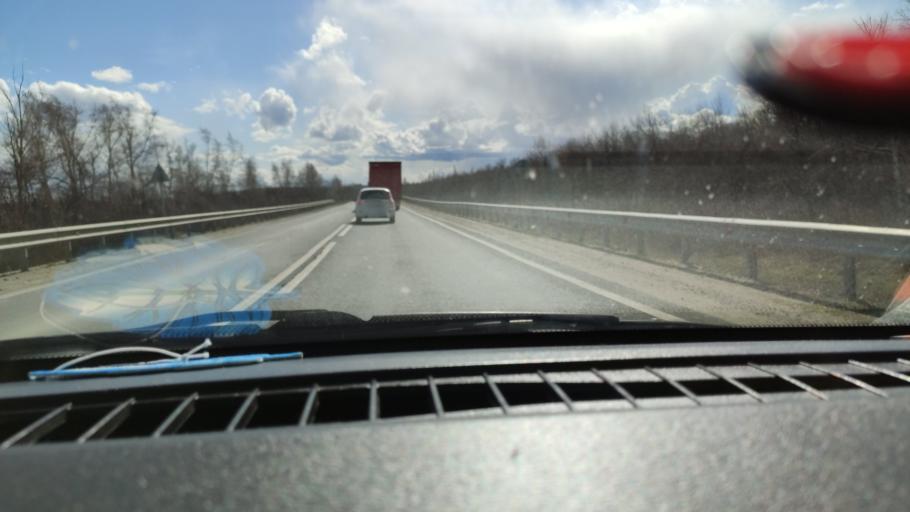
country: RU
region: Saratov
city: Dukhovnitskoye
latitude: 52.6741
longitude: 48.2253
